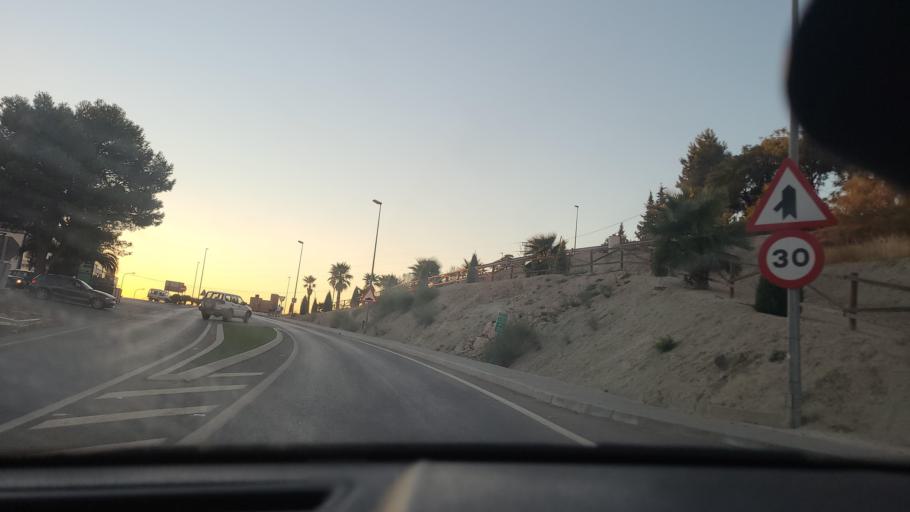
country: ES
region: Andalusia
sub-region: Provincia de Jaen
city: Jodar
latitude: 37.8269
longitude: -3.4144
